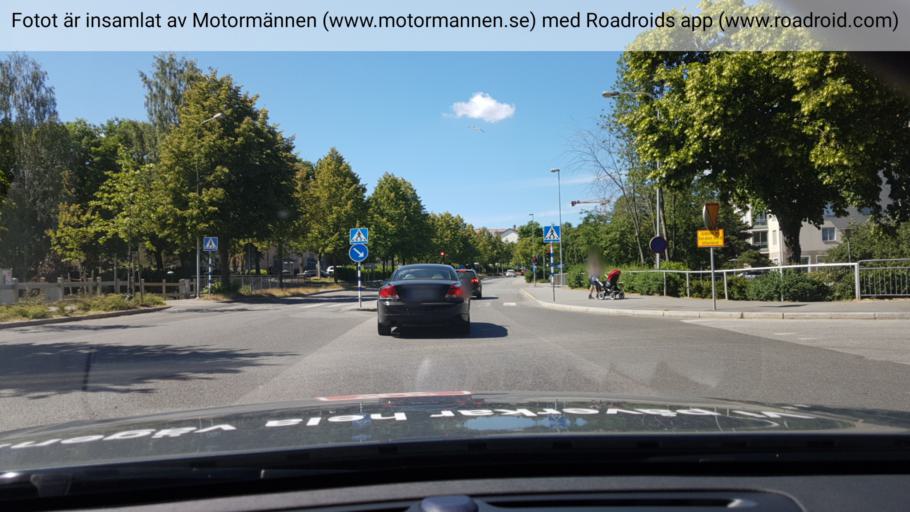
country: SE
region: Stockholm
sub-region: Tyreso Kommun
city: Bollmora
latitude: 59.2439
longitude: 18.2294
